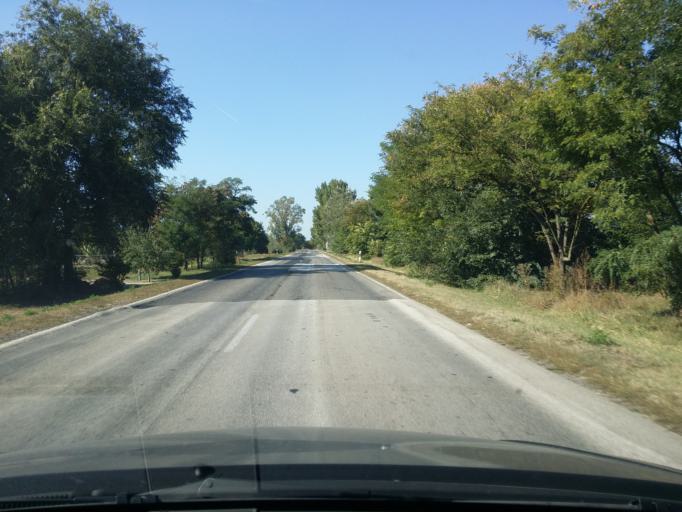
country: HU
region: Bacs-Kiskun
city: Lakitelek
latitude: 46.8815
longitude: 20.0026
